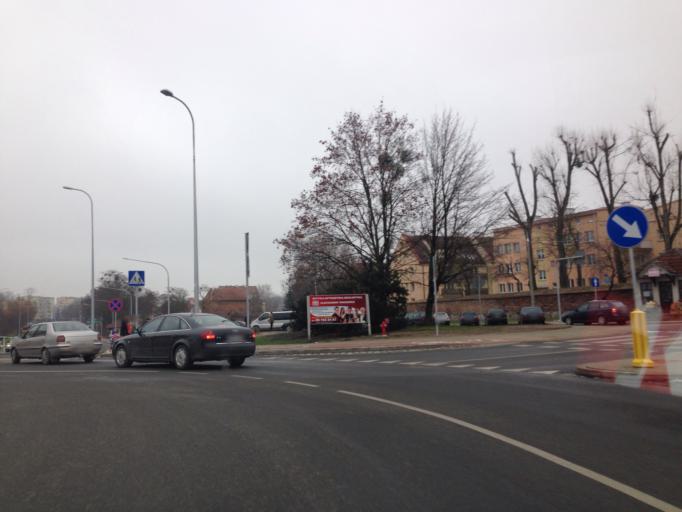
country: PL
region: Warmian-Masurian Voivodeship
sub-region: Powiat ketrzynski
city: Ketrzyn
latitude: 54.0763
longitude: 21.3752
